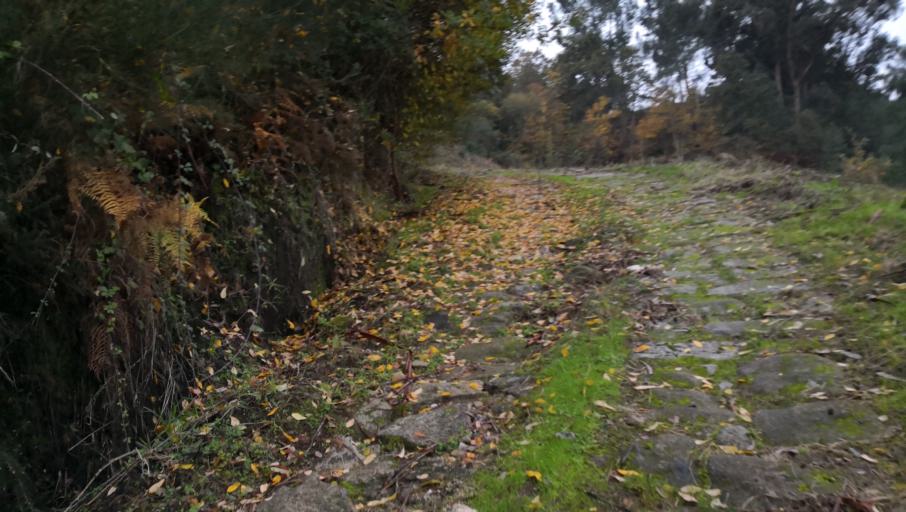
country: PT
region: Vila Real
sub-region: Vila Real
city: Vila Real
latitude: 41.2868
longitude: -7.7471
